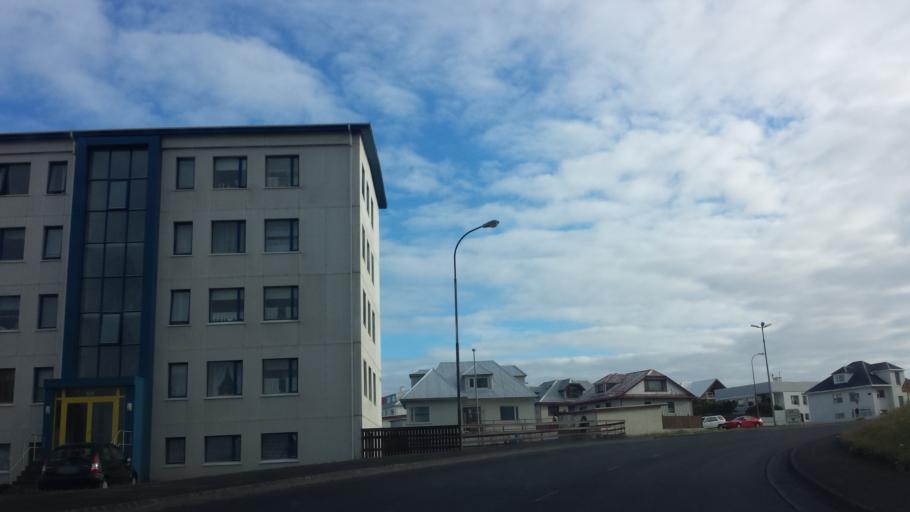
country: IS
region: South
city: Vestmannaeyjar
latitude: 63.4406
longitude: -20.2818
